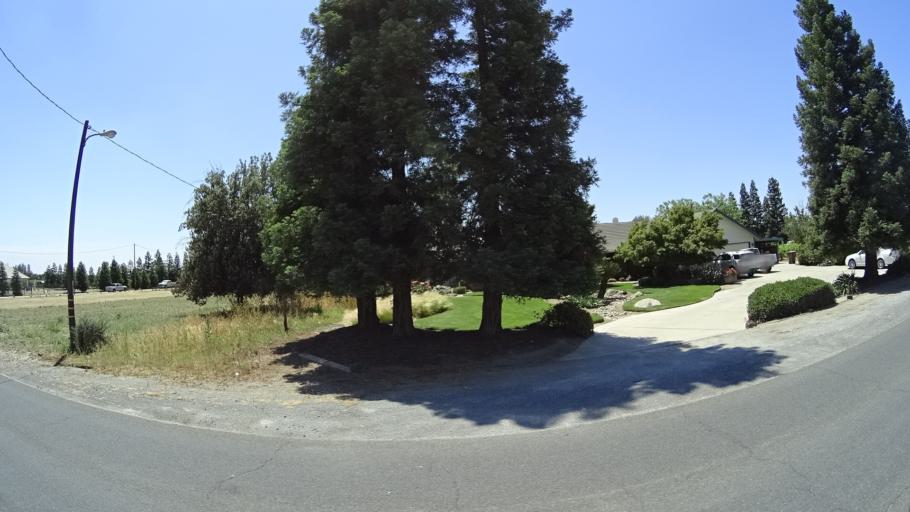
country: US
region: California
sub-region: Fresno County
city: Kingsburg
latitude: 36.4888
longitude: -119.5612
